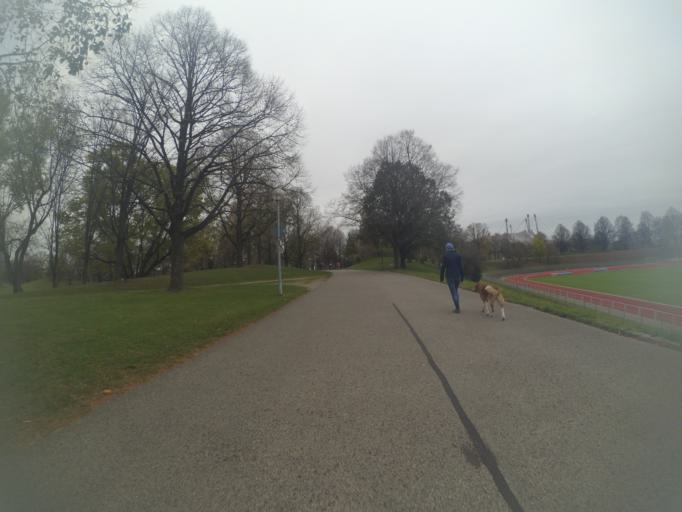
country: DE
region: Bavaria
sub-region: Upper Bavaria
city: Munich
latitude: 48.1787
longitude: 11.5474
